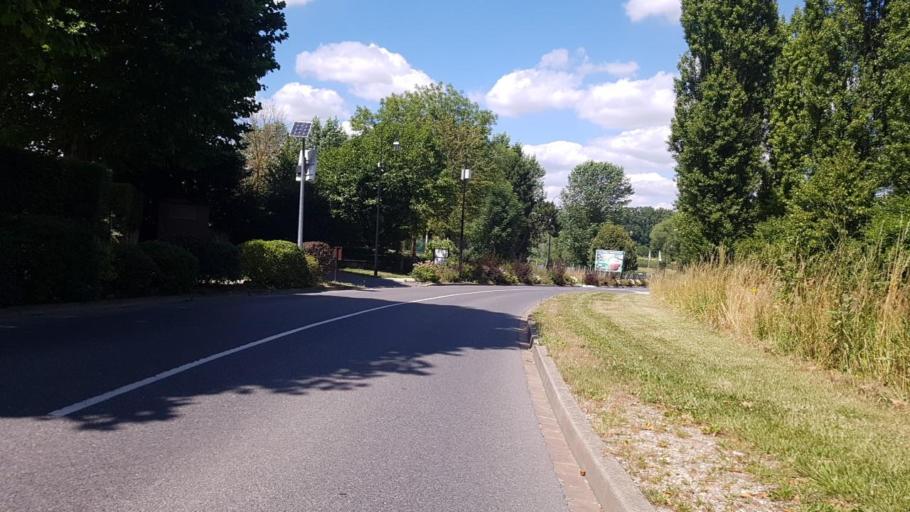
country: FR
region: Ile-de-France
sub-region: Departement de Seine-et-Marne
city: Juilly
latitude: 48.9953
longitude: 2.6645
